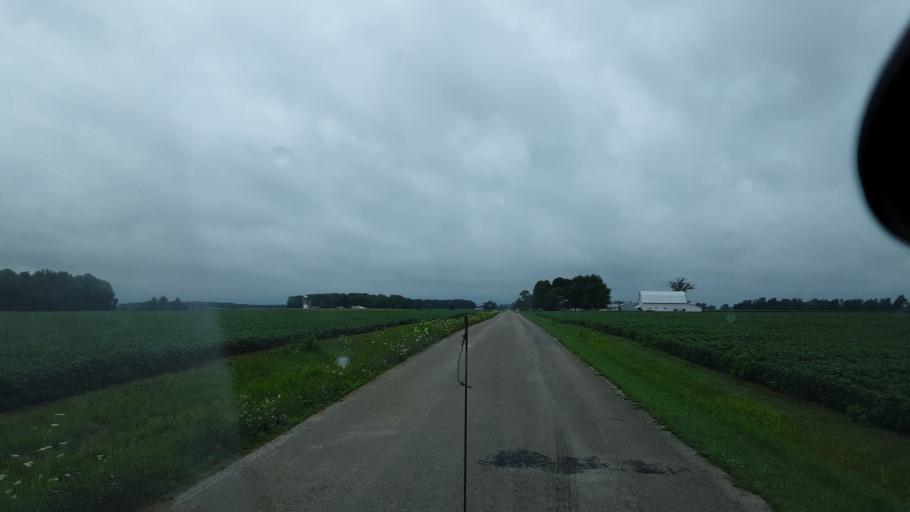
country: US
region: Indiana
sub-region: Adams County
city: Decatur
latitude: 40.8346
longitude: -84.8024
